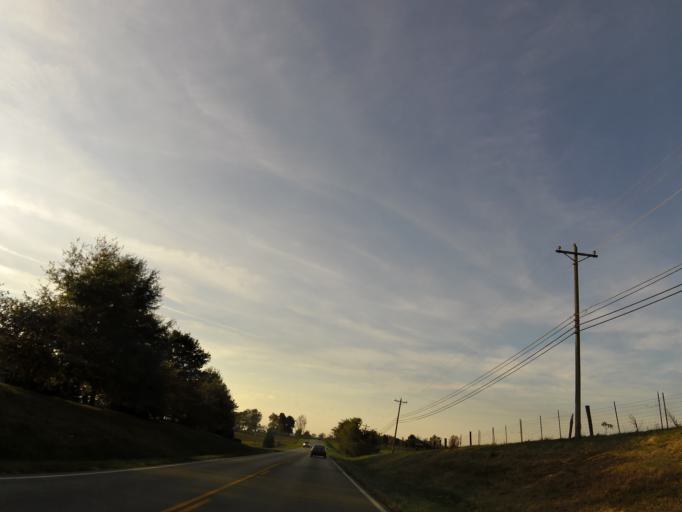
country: US
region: Kentucky
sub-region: Garrard County
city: Lancaster
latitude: 37.6552
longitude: -84.6074
